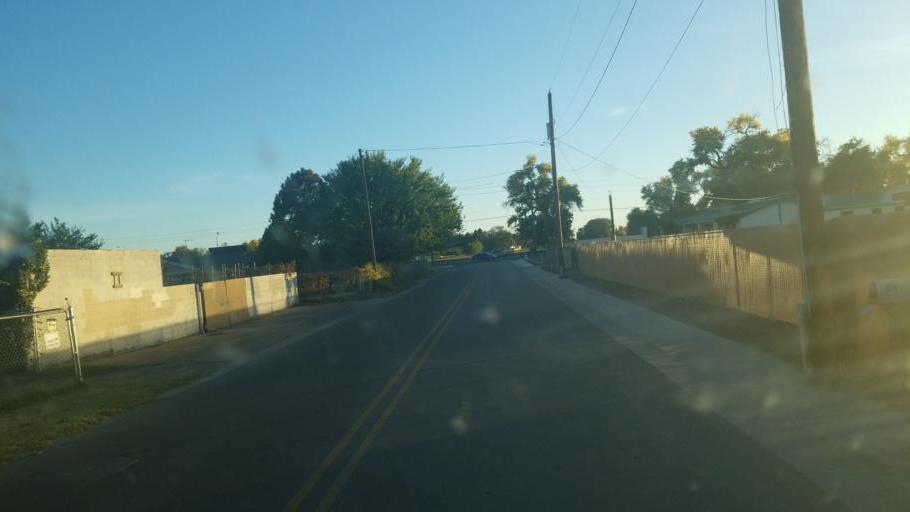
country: US
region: New Mexico
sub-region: Valencia County
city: Valencia
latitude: 34.8039
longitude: -106.7112
